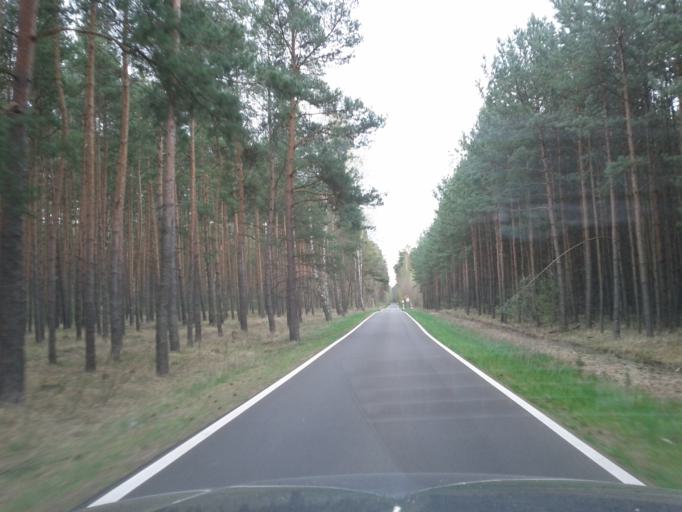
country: DE
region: Brandenburg
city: Spreenhagen
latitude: 52.3883
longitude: 13.8508
